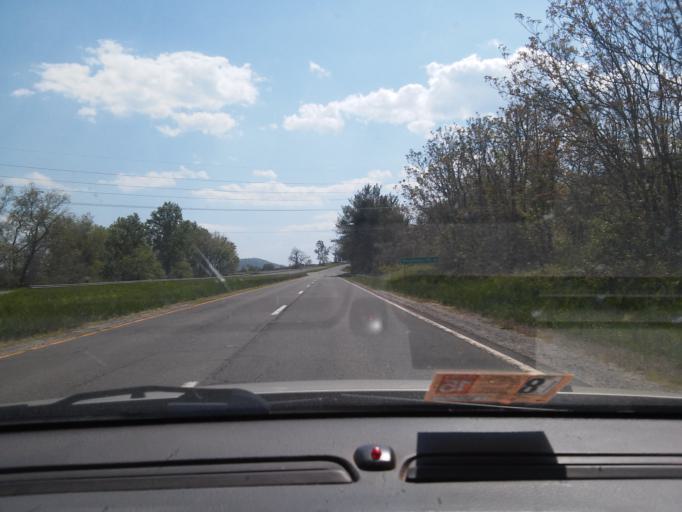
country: US
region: Virginia
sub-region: Rappahannock County
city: Washington
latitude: 38.7004
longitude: -78.1619
